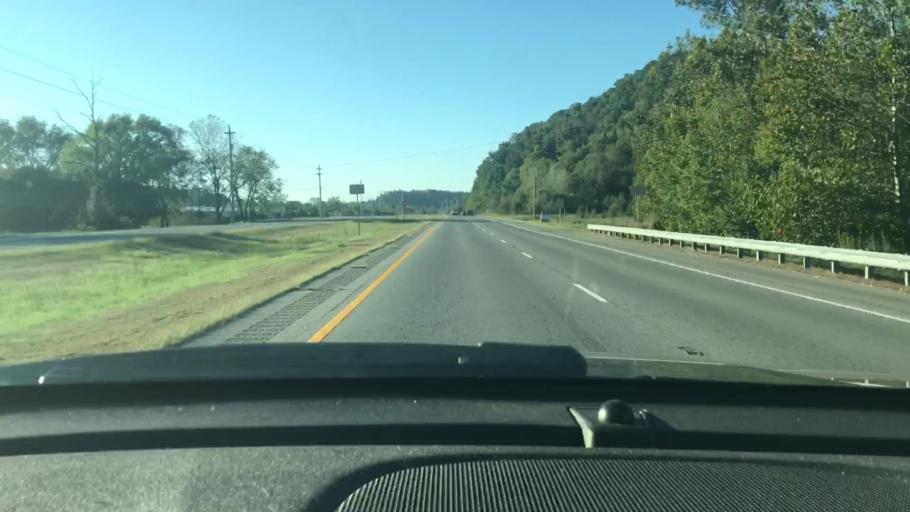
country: US
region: Tennessee
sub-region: Cheatham County
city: Ashland City
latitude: 36.2461
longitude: -87.0276
